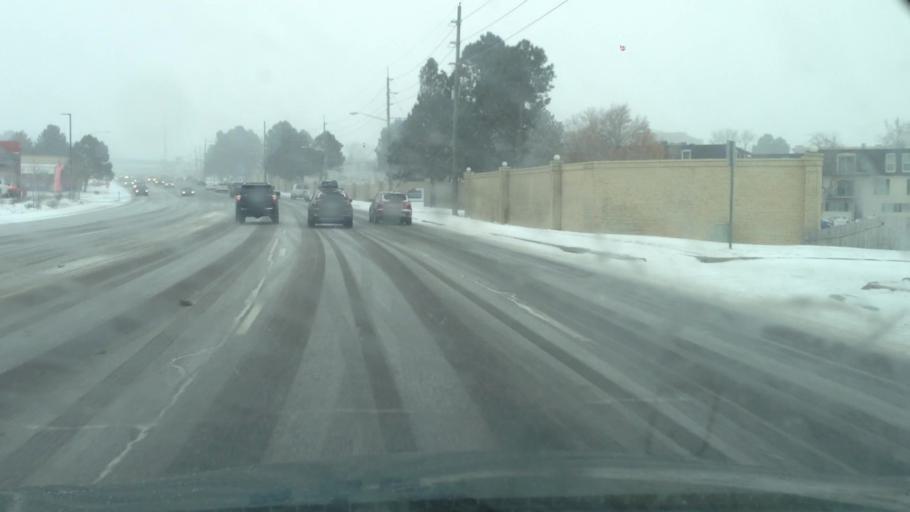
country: US
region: Colorado
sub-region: Adams County
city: Aurora
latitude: 39.6603
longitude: -104.8546
